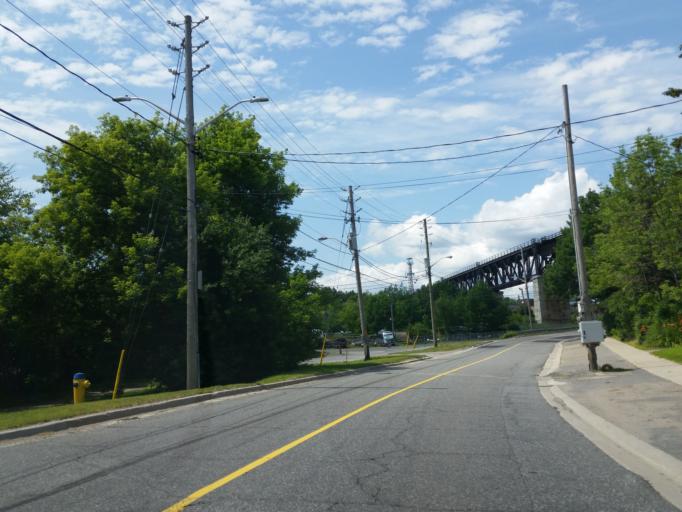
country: CA
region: Ontario
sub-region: Parry Sound District
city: Parry Sound
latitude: 45.3393
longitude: -80.0310
